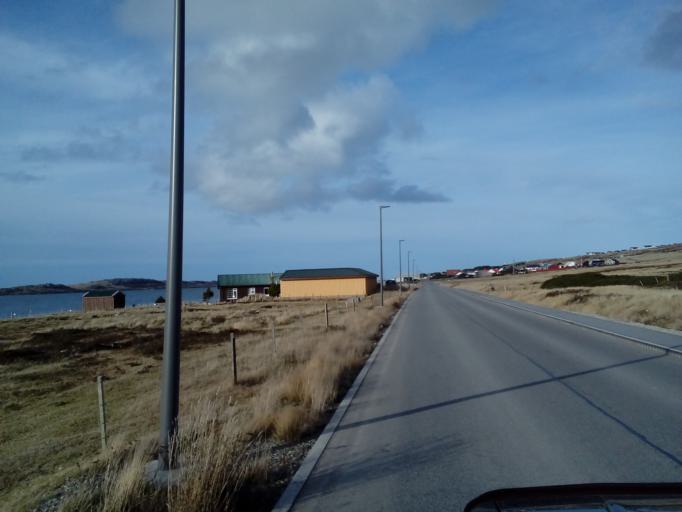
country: FK
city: Stanley
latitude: -51.6892
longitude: -57.8994
